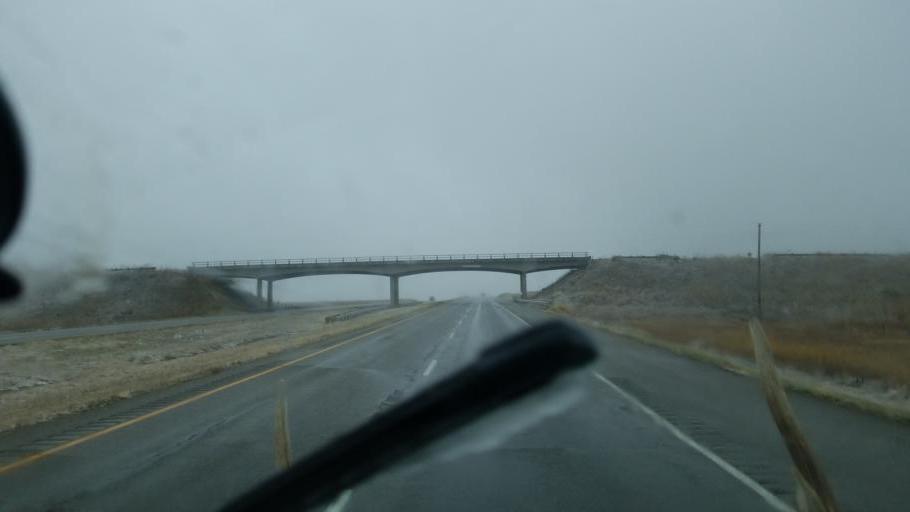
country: US
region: Colorado
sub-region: Pueblo County
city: Colorado City
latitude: 37.8930
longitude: -104.8288
